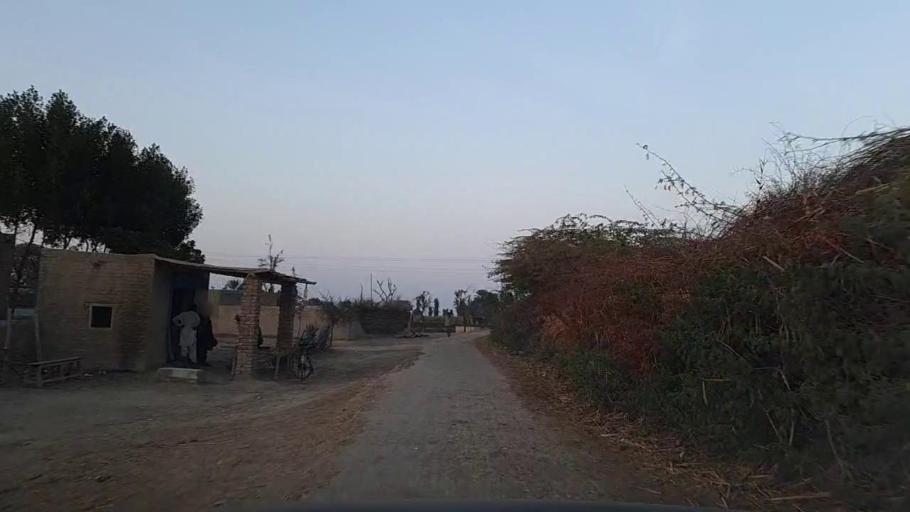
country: PK
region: Sindh
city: Tando Mittha Khan
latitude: 25.9425
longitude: 69.1445
